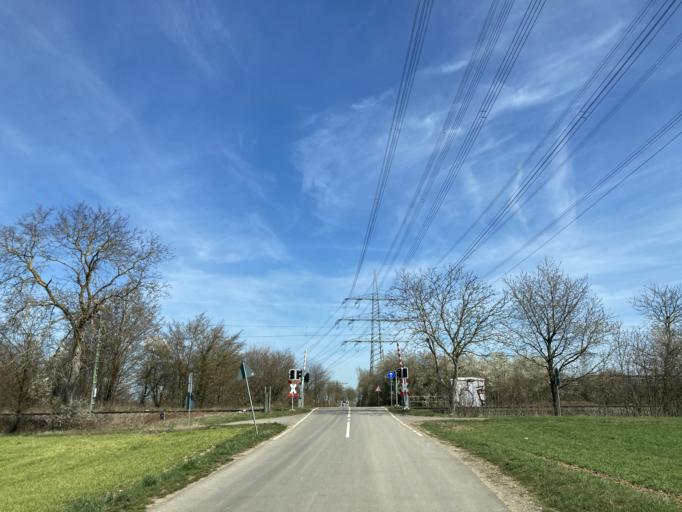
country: DE
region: Baden-Wuerttemberg
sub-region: Freiburg Region
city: Auggen
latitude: 47.8041
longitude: 7.5867
